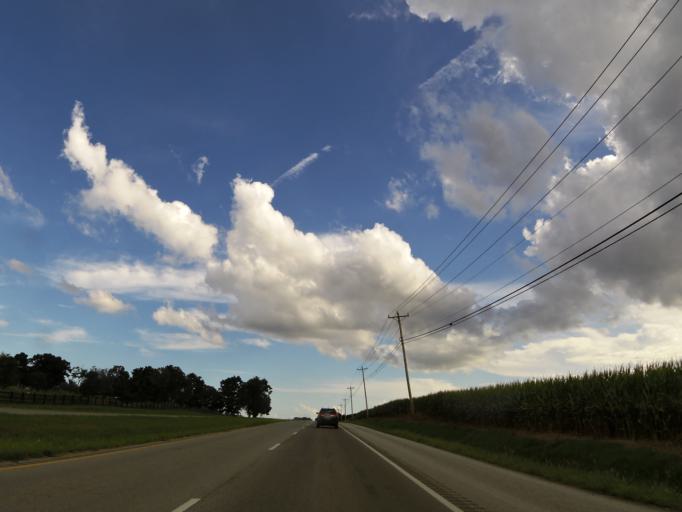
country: US
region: Kentucky
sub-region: Christian County
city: Hopkinsville
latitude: 36.7801
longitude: -87.4735
